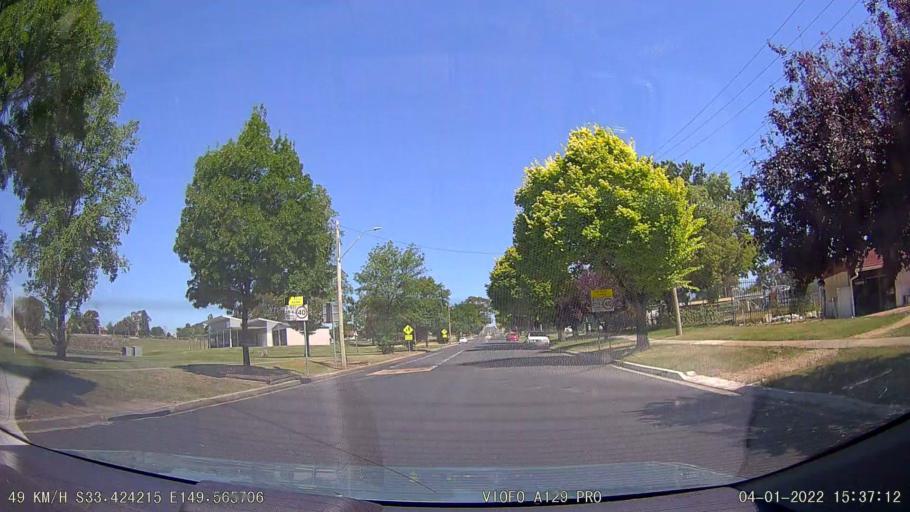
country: AU
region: New South Wales
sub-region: Bathurst Regional
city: Bathurst
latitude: -33.4240
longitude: 149.5655
